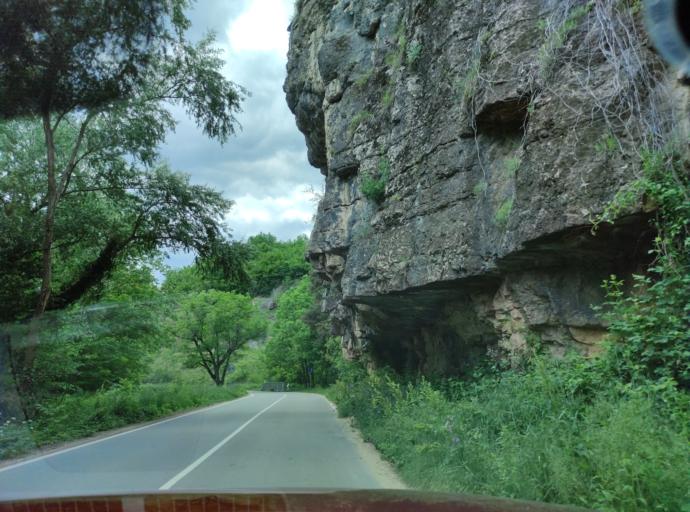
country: BG
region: Montana
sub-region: Obshtina Chiprovtsi
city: Chiprovtsi
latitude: 43.4428
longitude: 22.9333
